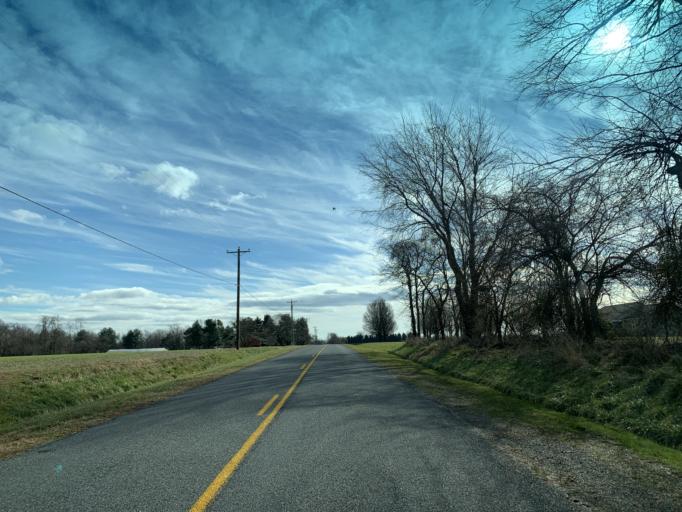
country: US
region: Maryland
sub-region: Kent County
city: Chestertown
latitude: 39.3412
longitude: -76.0507
